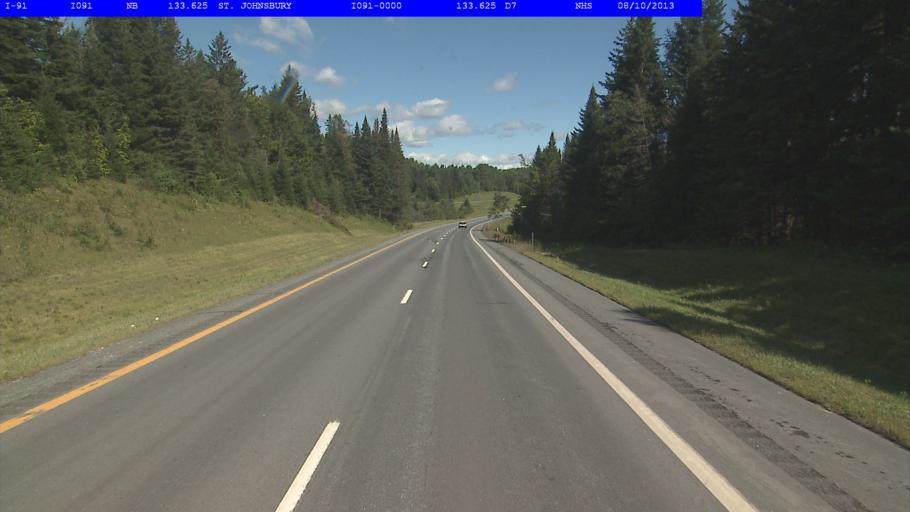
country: US
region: Vermont
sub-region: Caledonia County
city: St Johnsbury
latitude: 44.4691
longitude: -72.0243
